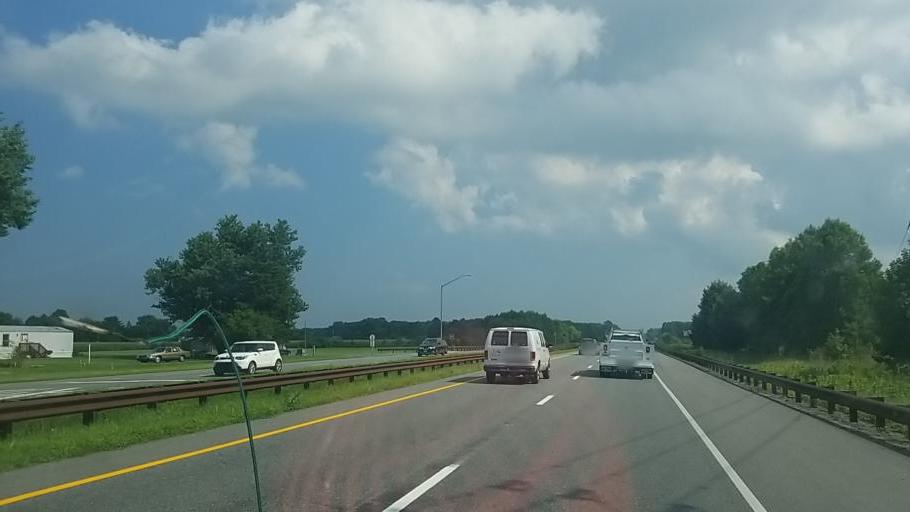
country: US
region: Delaware
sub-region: Sussex County
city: Selbyville
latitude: 38.4343
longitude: -75.2228
